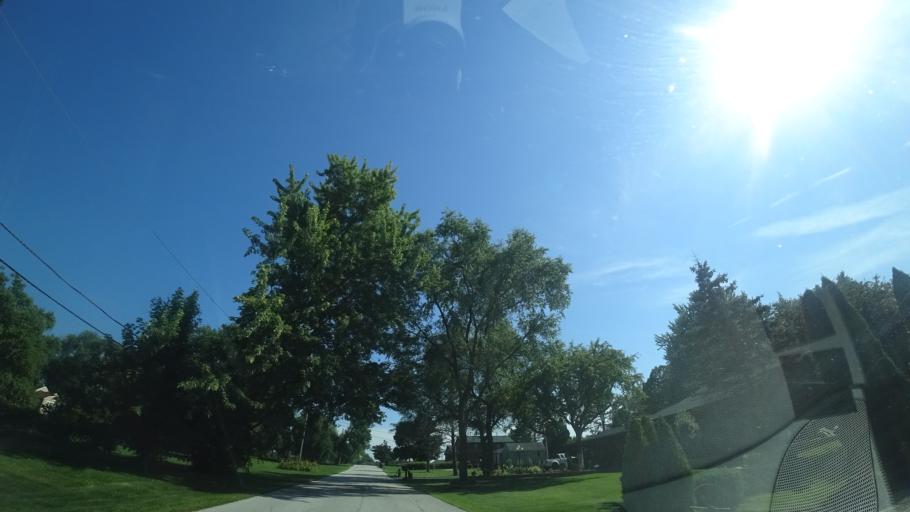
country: US
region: Illinois
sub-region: Cook County
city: Orland Hills
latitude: 41.5732
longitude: -87.8870
